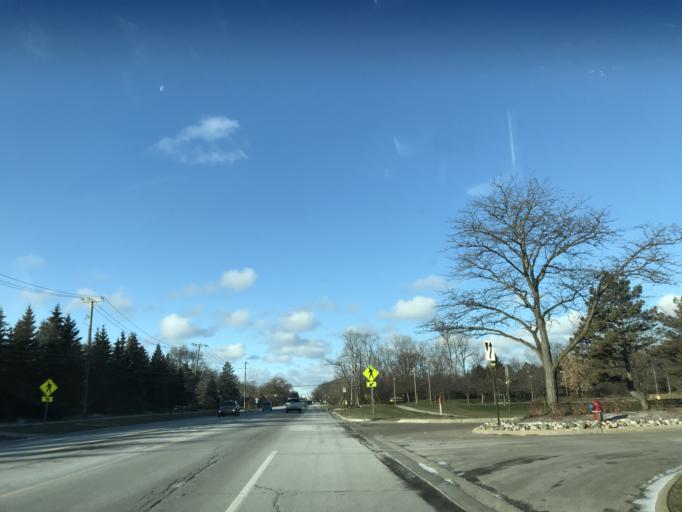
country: US
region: Michigan
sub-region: Oakland County
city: Troy
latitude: 42.5769
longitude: -83.1621
